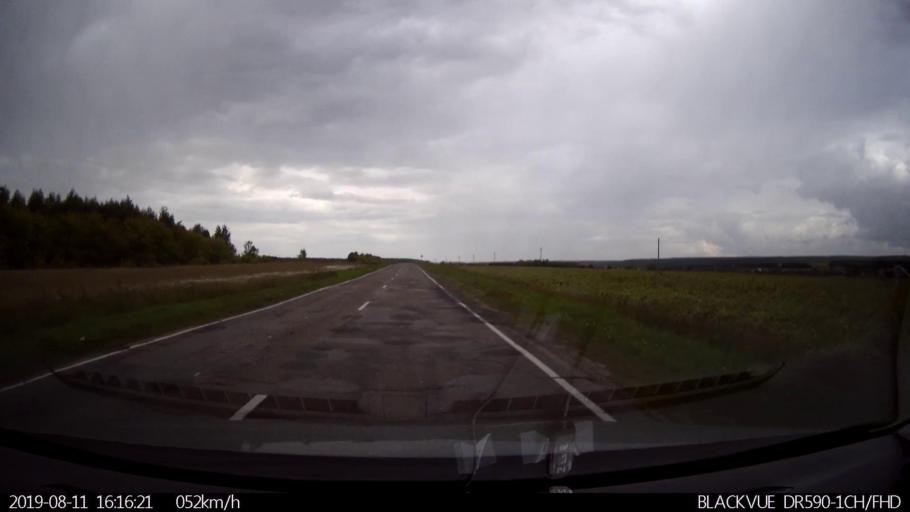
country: RU
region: Ulyanovsk
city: Mayna
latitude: 54.0404
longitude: 47.6218
